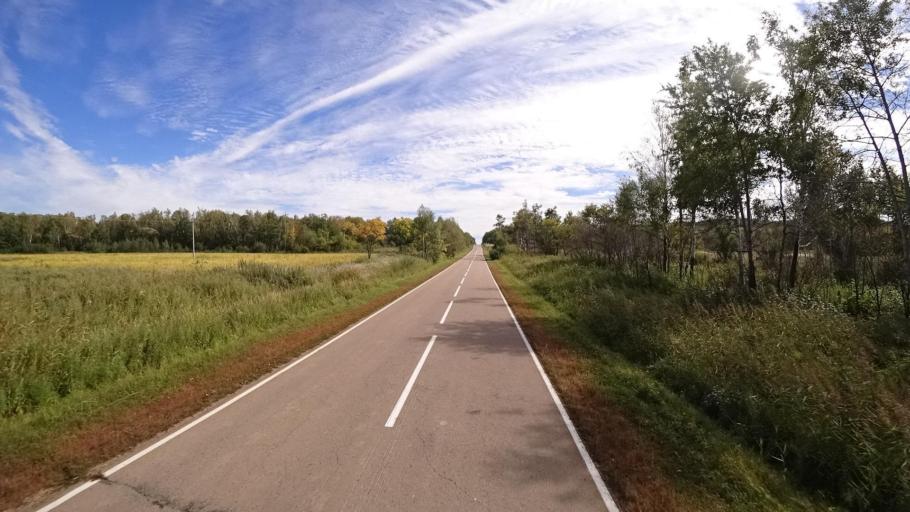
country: RU
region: Primorskiy
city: Yakovlevka
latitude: 44.4090
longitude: 133.5898
